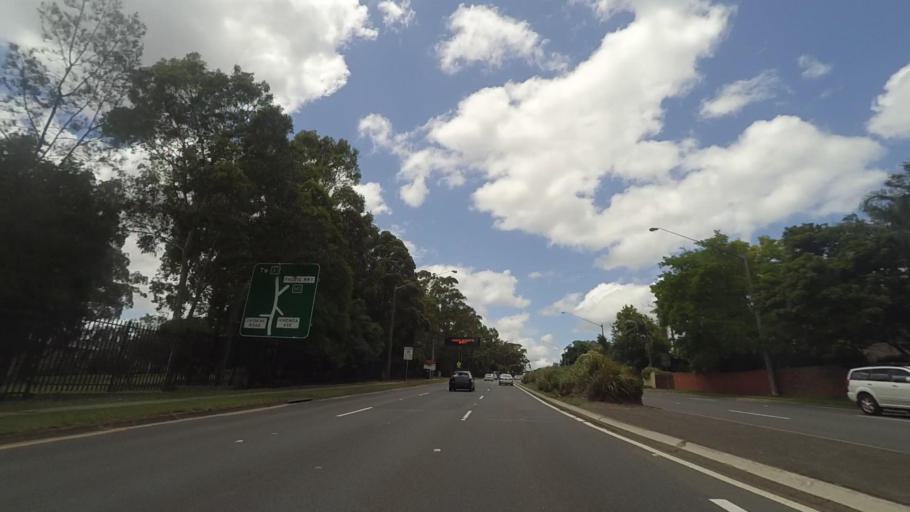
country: AU
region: New South Wales
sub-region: Ku-ring-gai
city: Normanhurst
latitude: -33.7230
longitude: 151.1012
